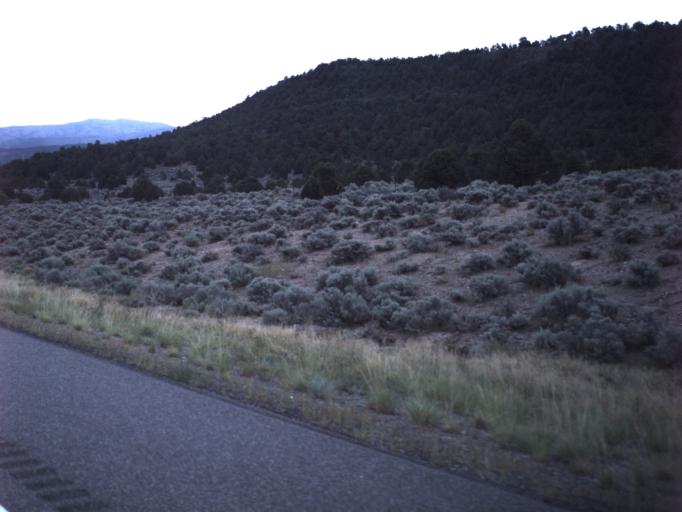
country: US
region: Utah
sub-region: Sevier County
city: Monroe
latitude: 38.5509
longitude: -112.3978
